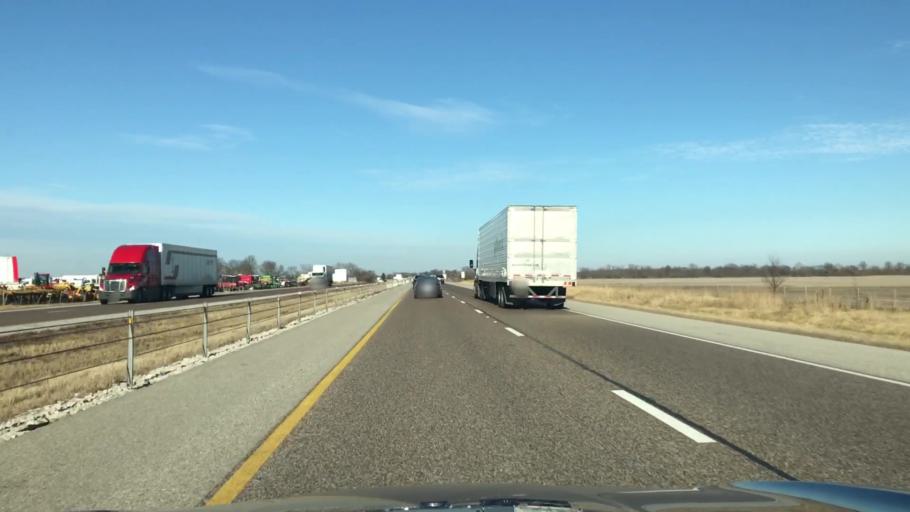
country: US
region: Illinois
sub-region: Madison County
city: Worden
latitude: 38.8946
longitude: -89.8345
